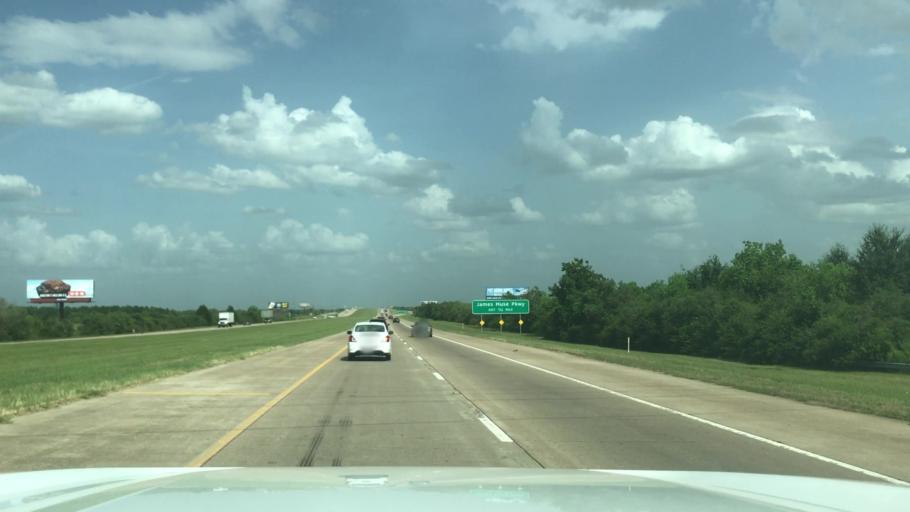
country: US
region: Texas
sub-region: Waller County
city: Prairie View
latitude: 30.0799
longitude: -95.9819
